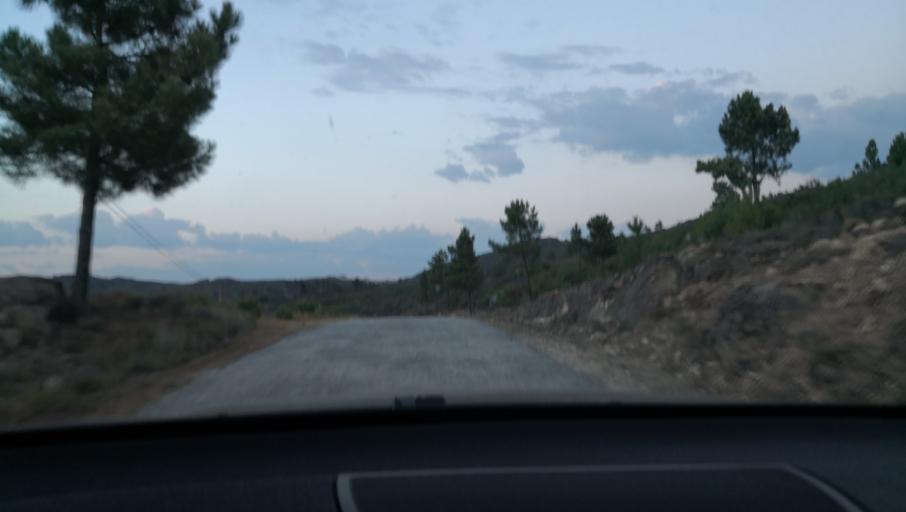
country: PT
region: Vila Real
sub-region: Sabrosa
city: Sabrosa
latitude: 41.2771
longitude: -7.6260
